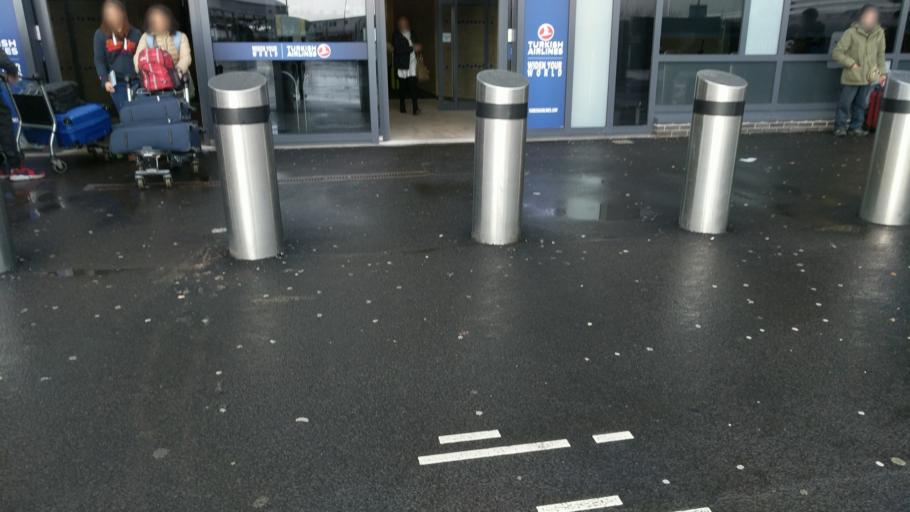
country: GB
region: Scotland
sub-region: Edinburgh
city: Ratho
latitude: 55.9482
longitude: -3.3616
